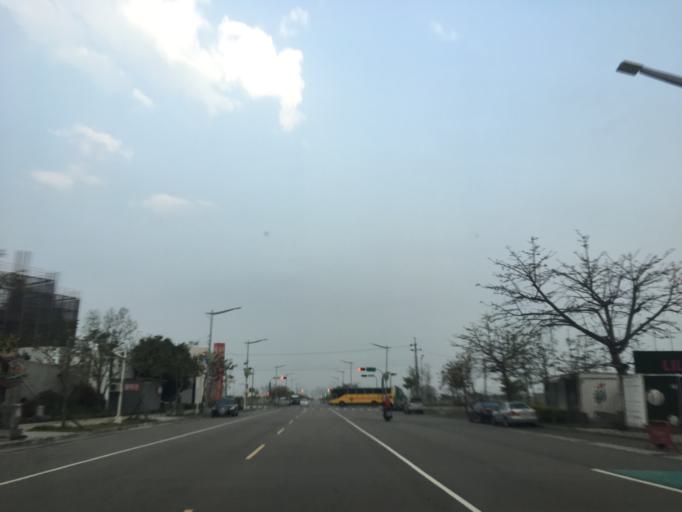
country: TW
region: Taiwan
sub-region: Taichung City
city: Taichung
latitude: 24.1979
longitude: 120.6844
